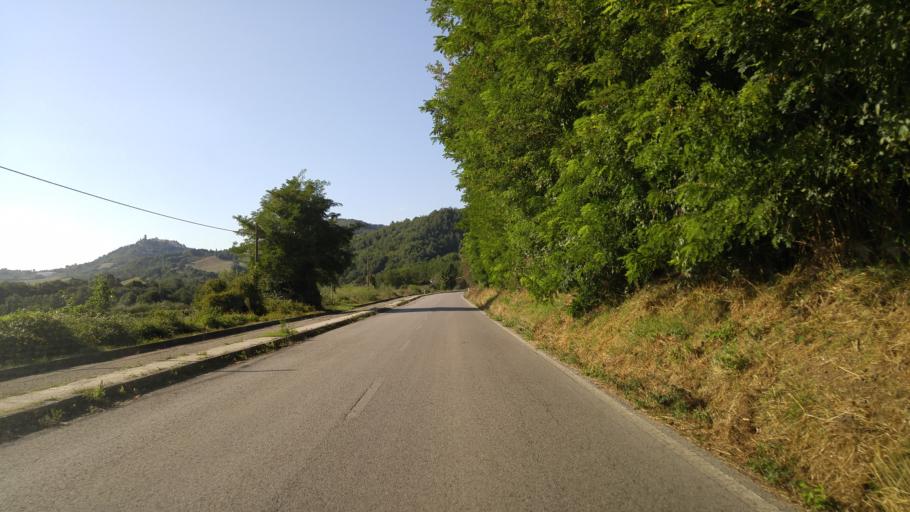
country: IT
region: The Marches
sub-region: Provincia di Pesaro e Urbino
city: Urbania
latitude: 43.6783
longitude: 12.5216
